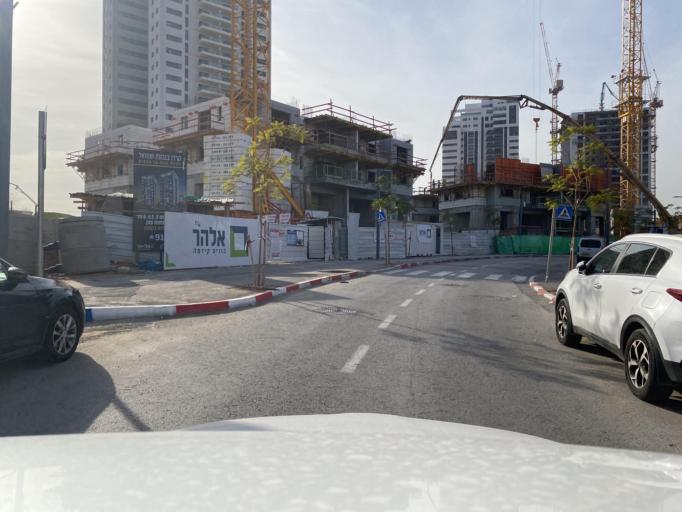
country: IL
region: Tel Aviv
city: Giv`at Shemu'el
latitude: 32.0704
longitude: 34.8542
